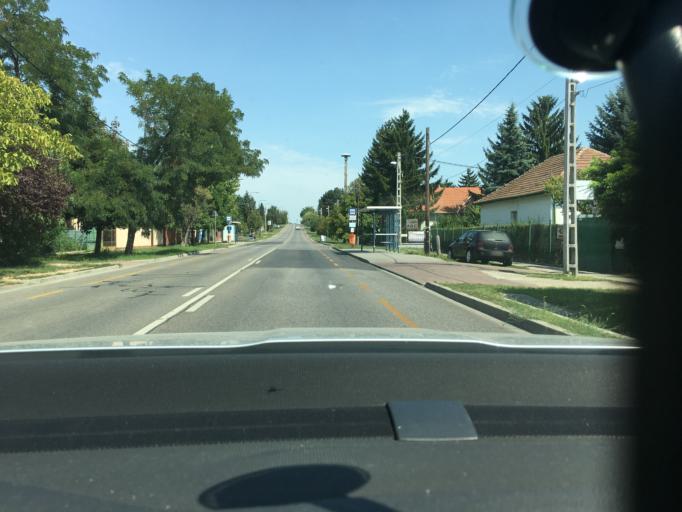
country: HU
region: Budapest
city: Budapest XVI. keruelet
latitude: 47.5101
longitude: 19.2123
